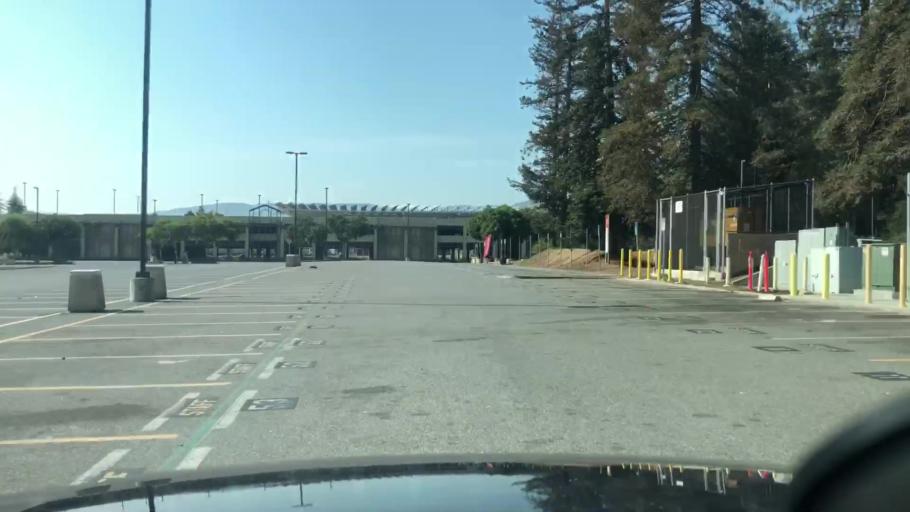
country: US
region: California
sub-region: Santa Clara County
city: Cupertino
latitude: 37.3207
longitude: -122.0432
